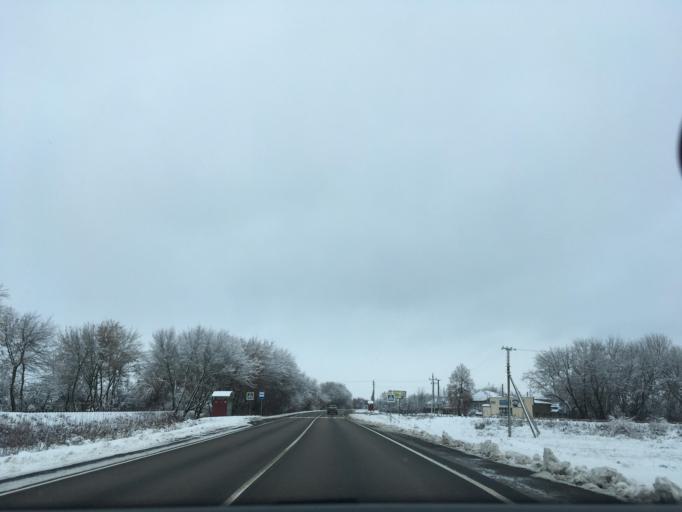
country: RU
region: Voronezj
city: Zabolotovka
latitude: 50.2467
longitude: 39.3539
